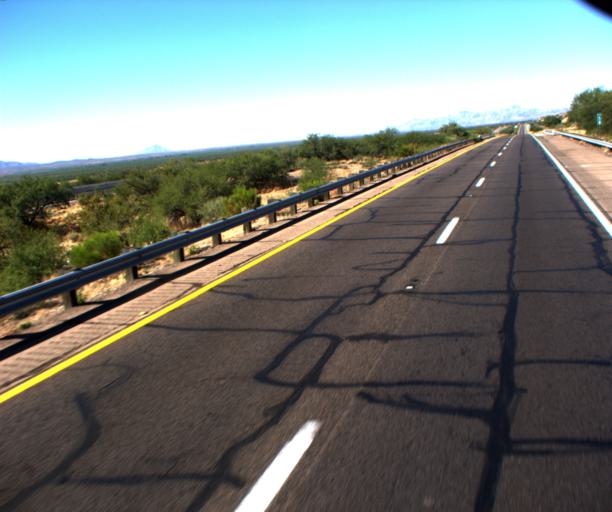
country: US
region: Arizona
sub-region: Pima County
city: Green Valley
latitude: 31.8053
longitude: -111.0137
